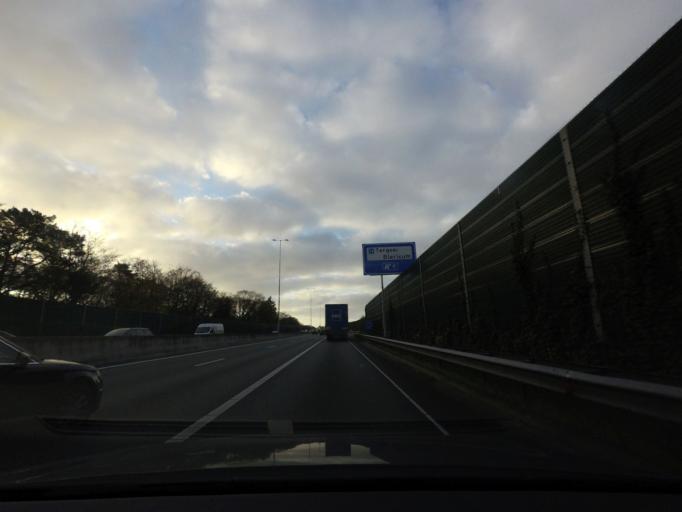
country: NL
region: North Holland
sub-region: Gemeente Laren
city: Laren
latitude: 52.2711
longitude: 5.1962
